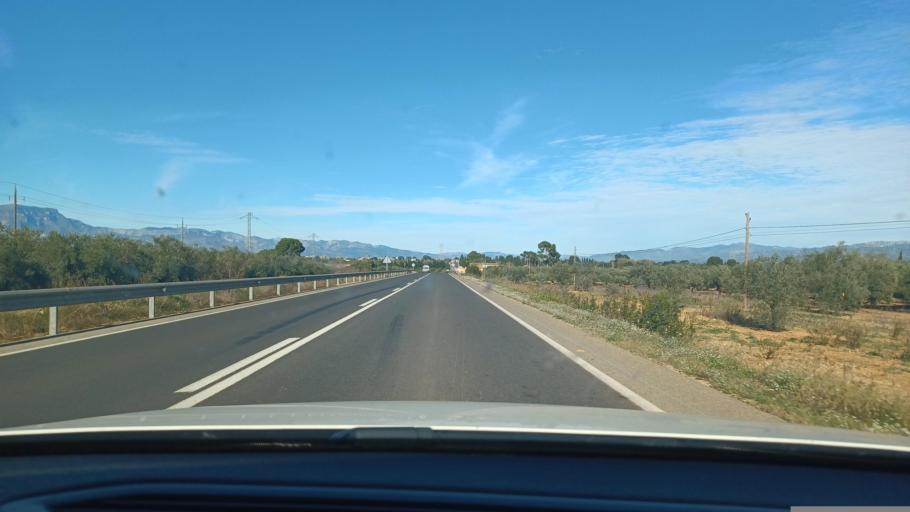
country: ES
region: Catalonia
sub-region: Provincia de Tarragona
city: Santa Barbara
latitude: 40.6941
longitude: 0.5058
